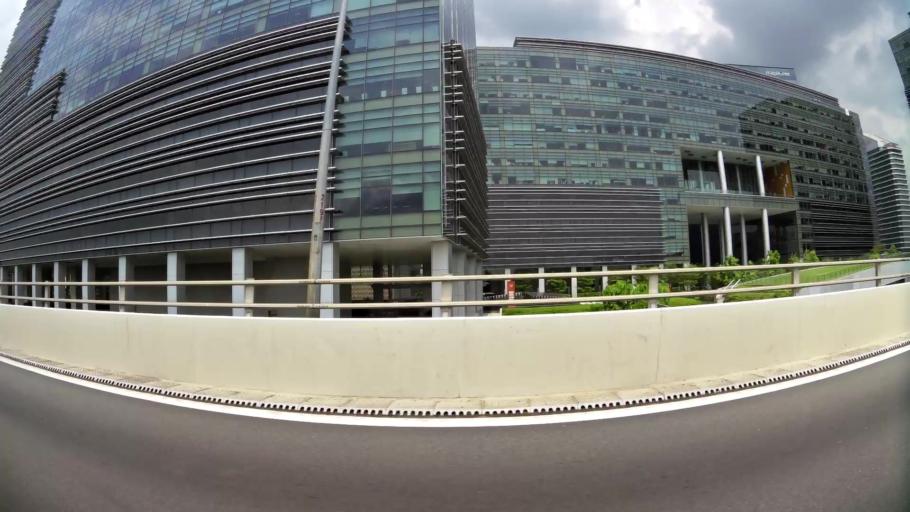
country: SG
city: Singapore
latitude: 1.2743
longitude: 103.7981
